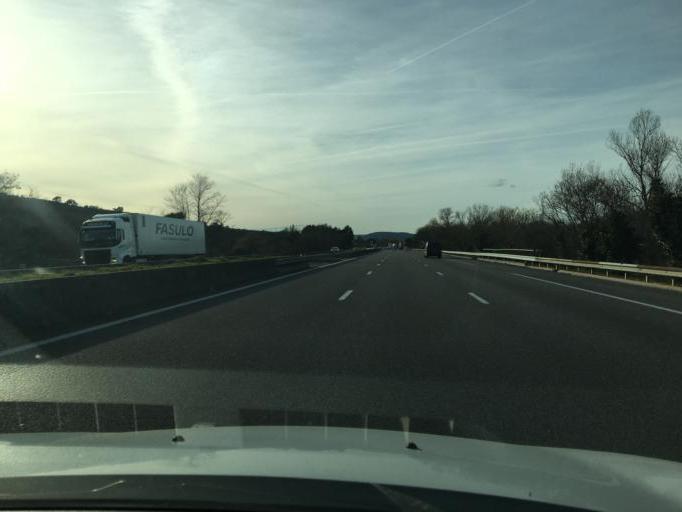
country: FR
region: Provence-Alpes-Cote d'Azur
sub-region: Departement du Var
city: Le Muy
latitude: 43.4628
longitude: 6.5842
